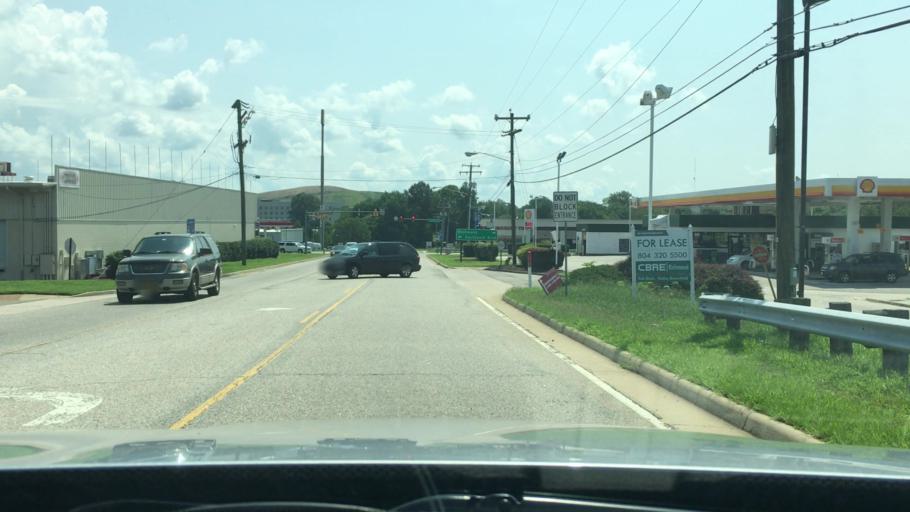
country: US
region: Virginia
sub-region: City of Petersburg
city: Petersburg
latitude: 37.2426
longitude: -77.3932
